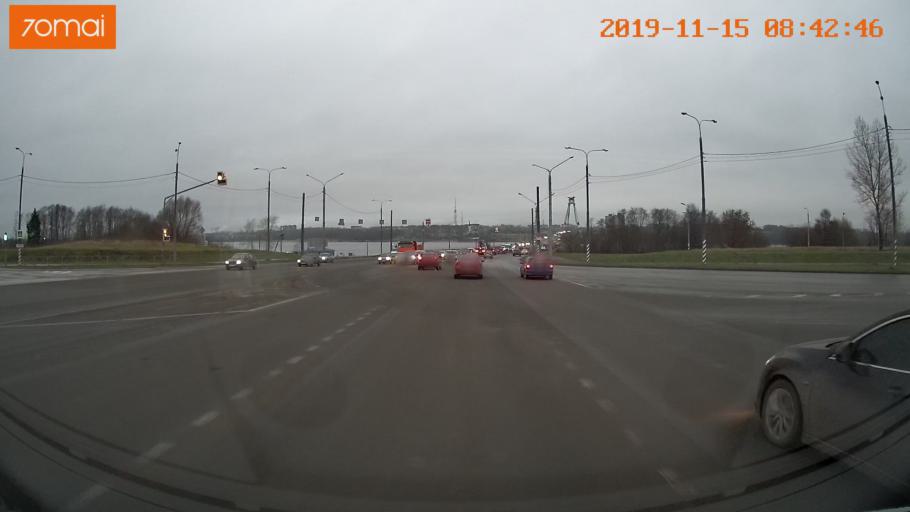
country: RU
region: Vologda
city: Cherepovets
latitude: 59.1053
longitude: 37.9064
